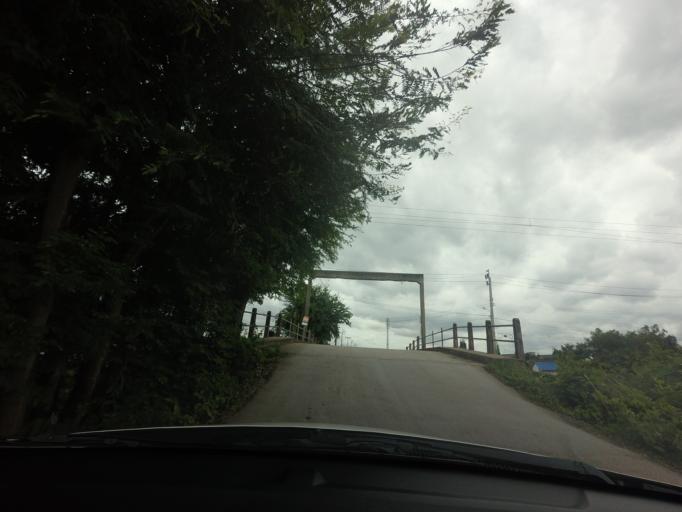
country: TH
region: Bangkok
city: Min Buri
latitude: 13.7754
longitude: 100.7688
